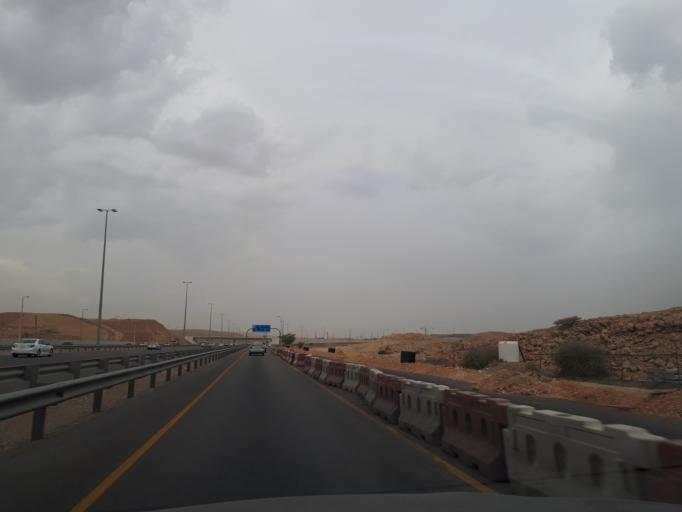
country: OM
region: Muhafazat Masqat
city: Bawshar
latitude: 23.5629
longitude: 58.3461
